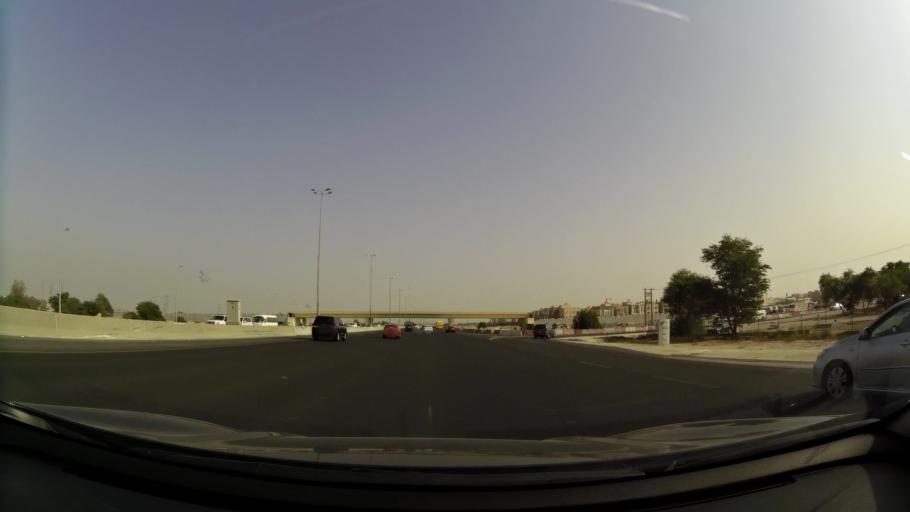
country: KW
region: Muhafazat al Jahra'
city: Al Jahra'
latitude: 29.3309
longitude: 47.7346
